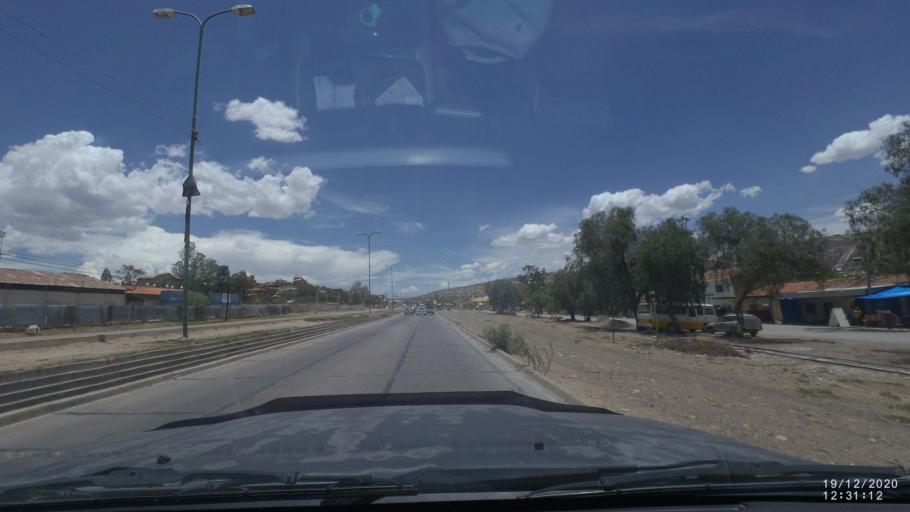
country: BO
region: Cochabamba
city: Cochabamba
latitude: -17.4573
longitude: -66.1250
